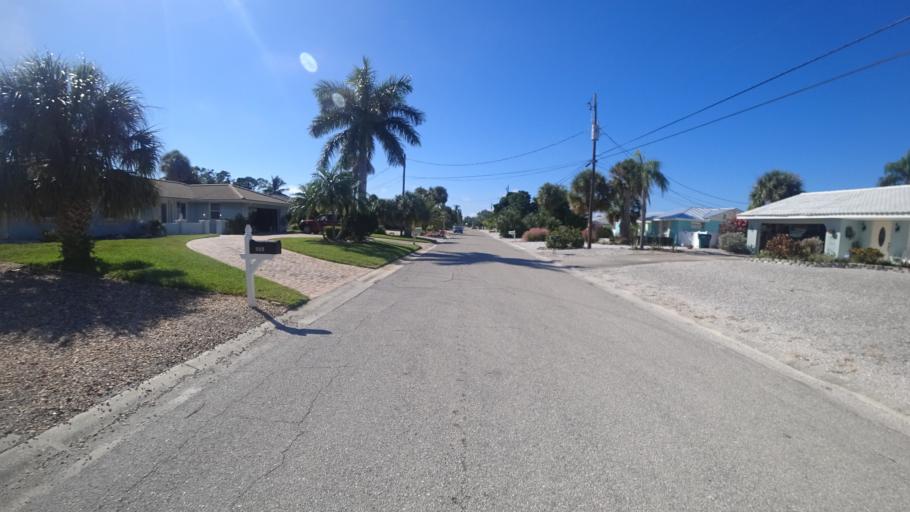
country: US
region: Florida
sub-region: Manatee County
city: Anna Maria
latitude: 27.5221
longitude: -82.7099
